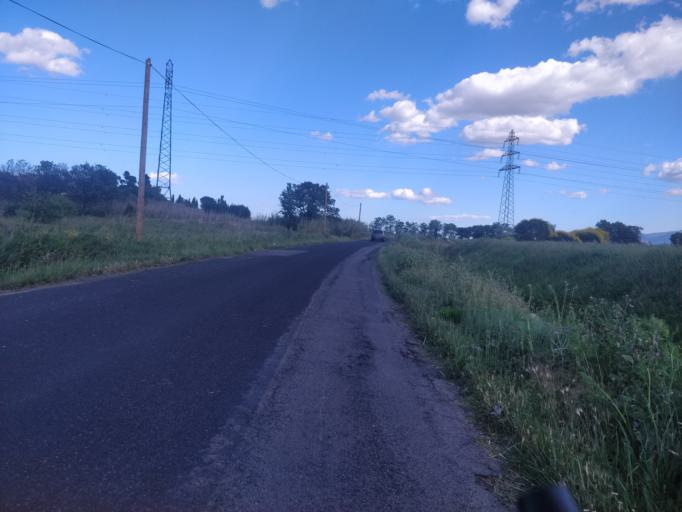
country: FR
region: Languedoc-Roussillon
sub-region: Departement des Pyrenees-Orientales
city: Cabestany
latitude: 42.6794
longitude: 2.9200
